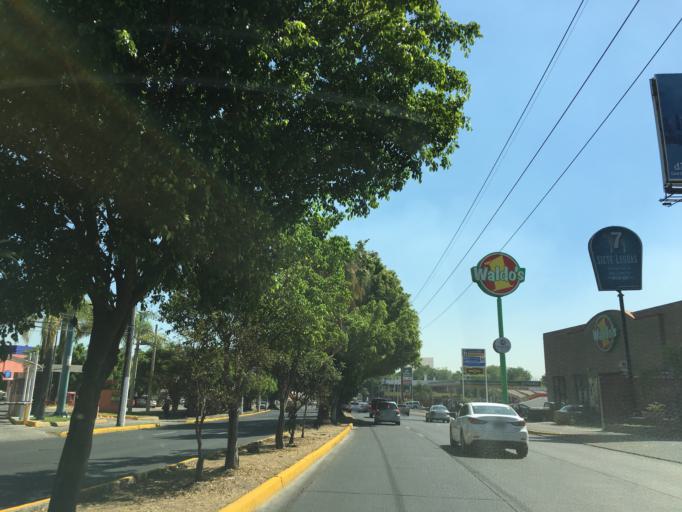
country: MX
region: Jalisco
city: Guadalajara
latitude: 20.6354
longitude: -103.3981
